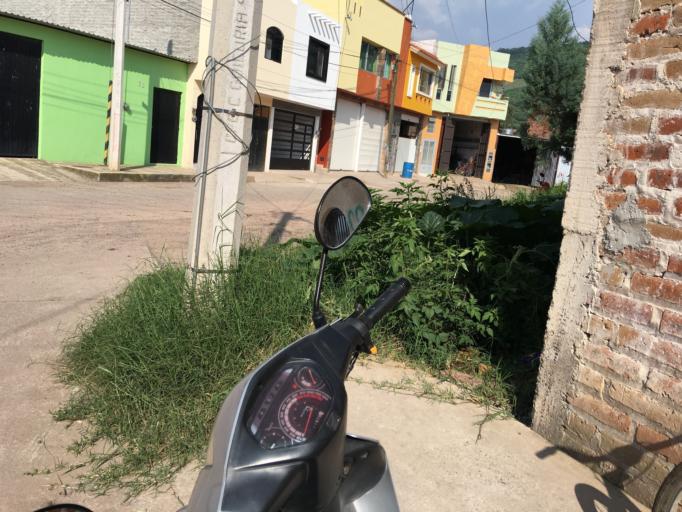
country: MX
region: Jalisco
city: Atotonilco el Alto
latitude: 20.5499
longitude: -102.4986
